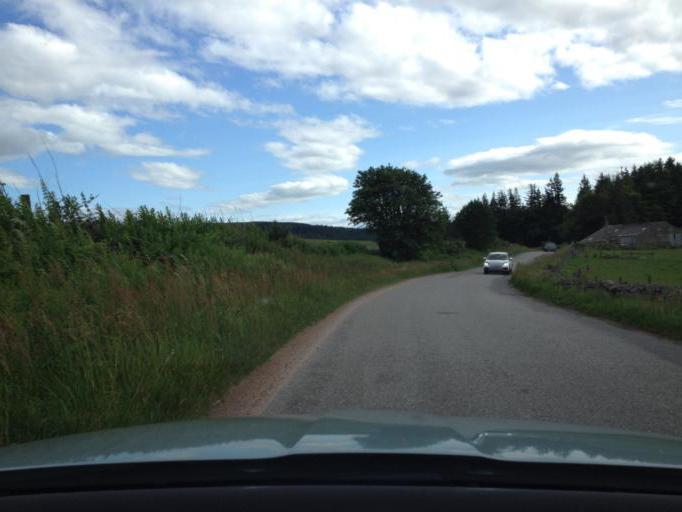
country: GB
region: Scotland
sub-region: Aberdeenshire
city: Banchory
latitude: 56.9804
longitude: -2.5729
